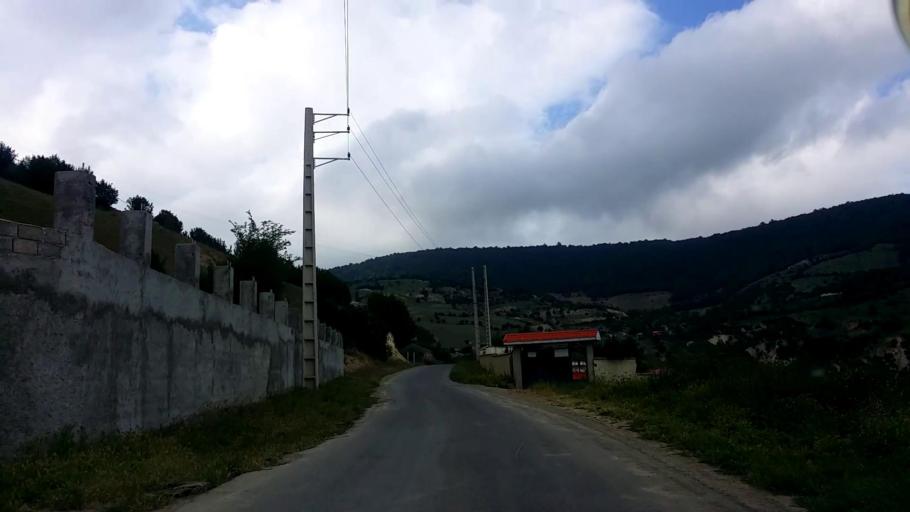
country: IR
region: Mazandaran
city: Chalus
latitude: 36.5500
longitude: 51.2700
